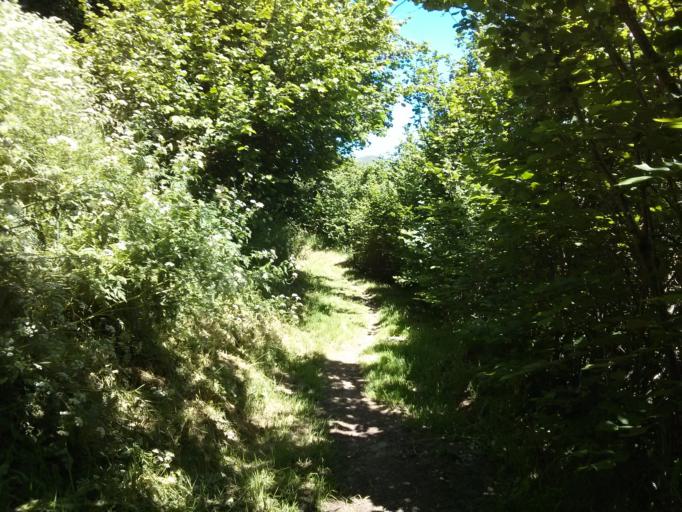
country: FR
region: Auvergne
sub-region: Departement du Puy-de-Dome
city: Mont-Dore
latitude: 45.5913
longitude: 2.8057
